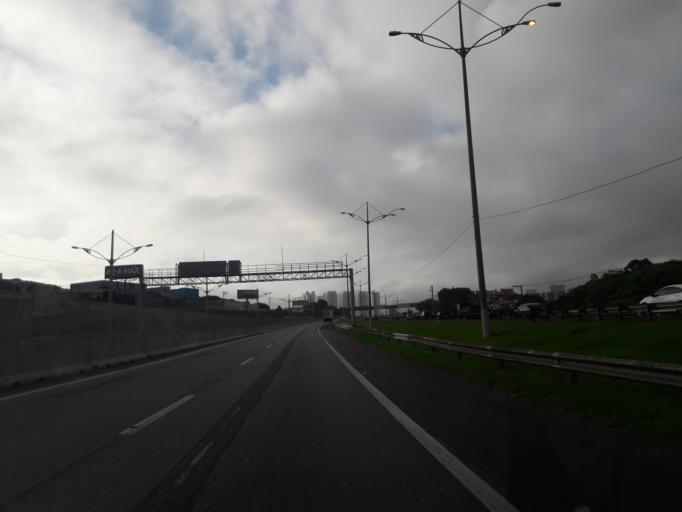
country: BR
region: Sao Paulo
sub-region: Sao Bernardo Do Campo
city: Sao Bernardo do Campo
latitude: -23.6980
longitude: -46.5620
